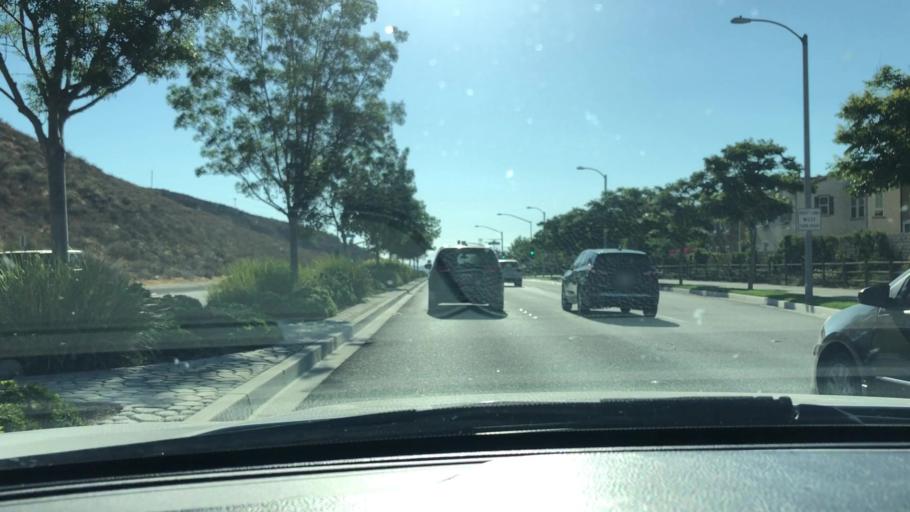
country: US
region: California
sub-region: Los Angeles County
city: Santa Clarita
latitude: 34.3972
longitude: -118.4897
